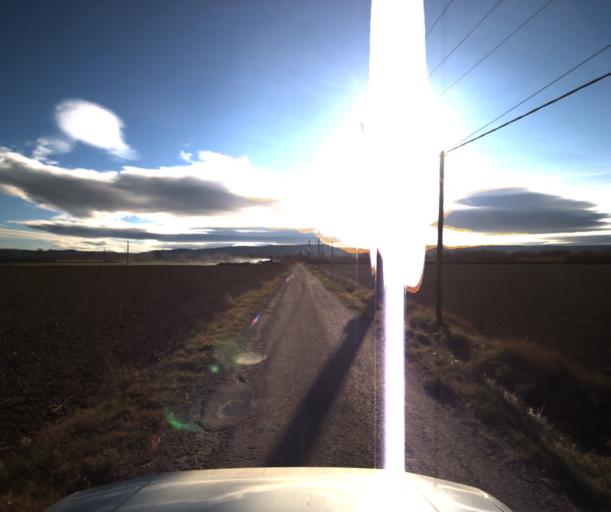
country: FR
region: Provence-Alpes-Cote d'Azur
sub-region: Departement du Vaucluse
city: Pertuis
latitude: 43.6869
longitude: 5.4666
